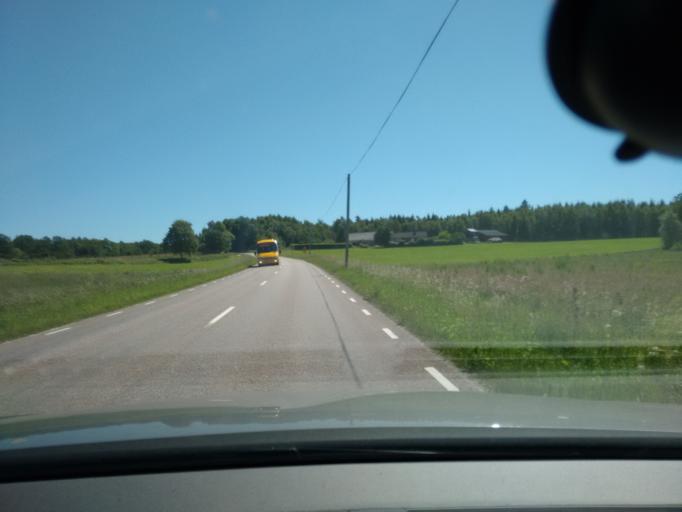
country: SE
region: Skane
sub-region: Horby Kommun
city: Hoerby
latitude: 55.7964
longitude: 13.8087
